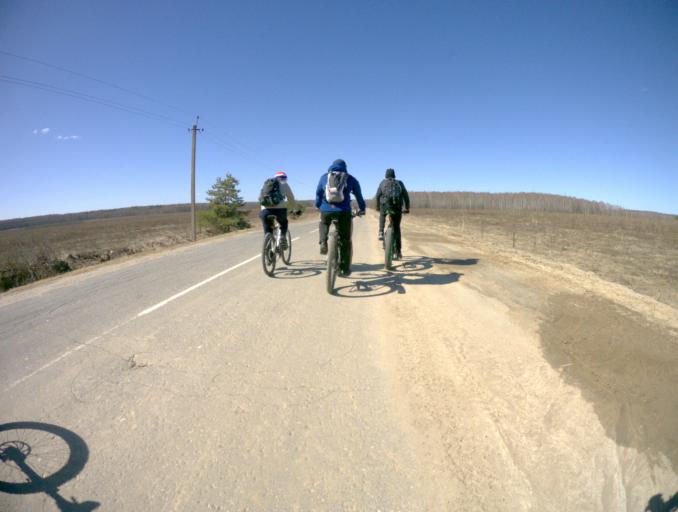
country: RU
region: Vladimir
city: Kameshkovo
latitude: 56.3468
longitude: 40.7962
